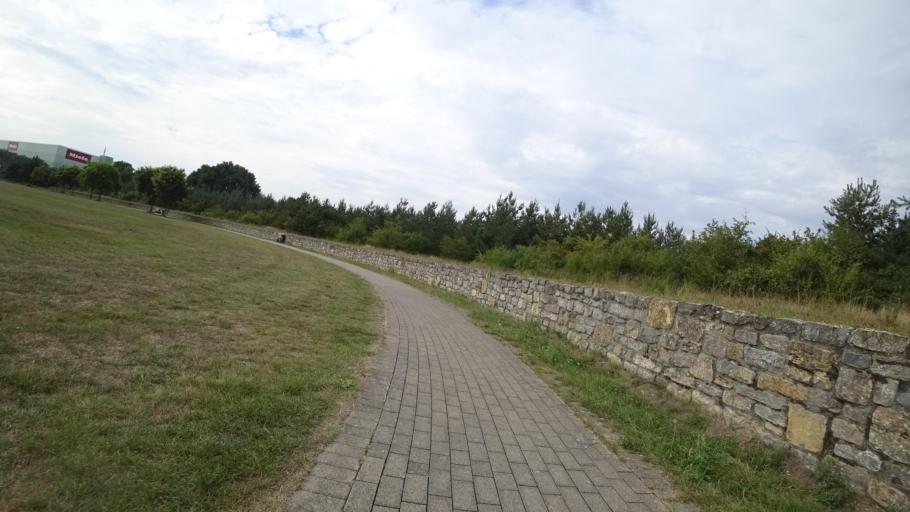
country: DE
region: North Rhine-Westphalia
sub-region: Regierungsbezirk Detmold
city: Guetersloh
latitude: 51.9171
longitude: 8.4119
